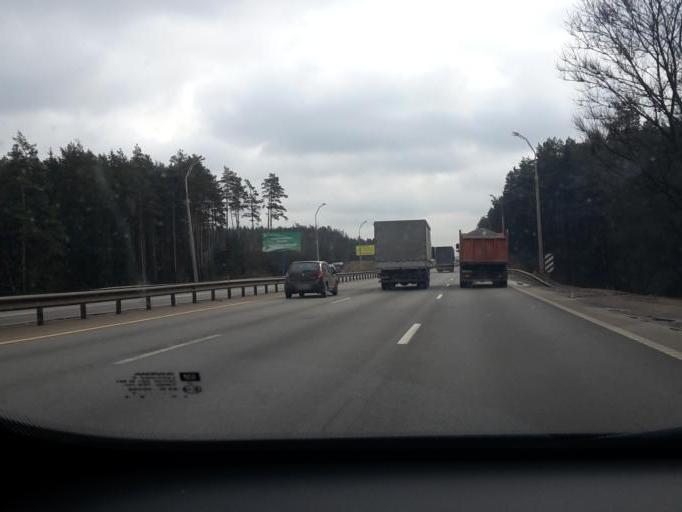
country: BY
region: Minsk
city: Borovlyany
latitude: 53.9528
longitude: 27.6464
